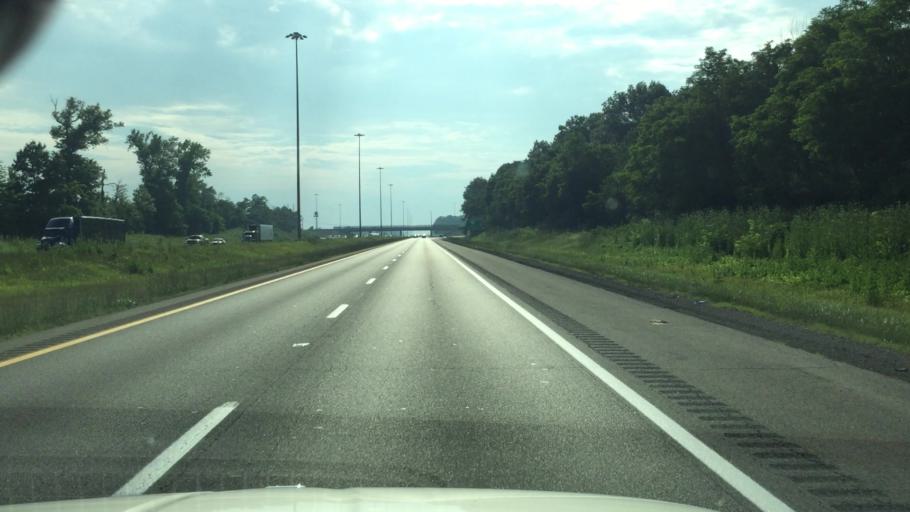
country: US
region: Ohio
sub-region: Licking County
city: Etna
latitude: 39.9484
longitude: -82.6736
